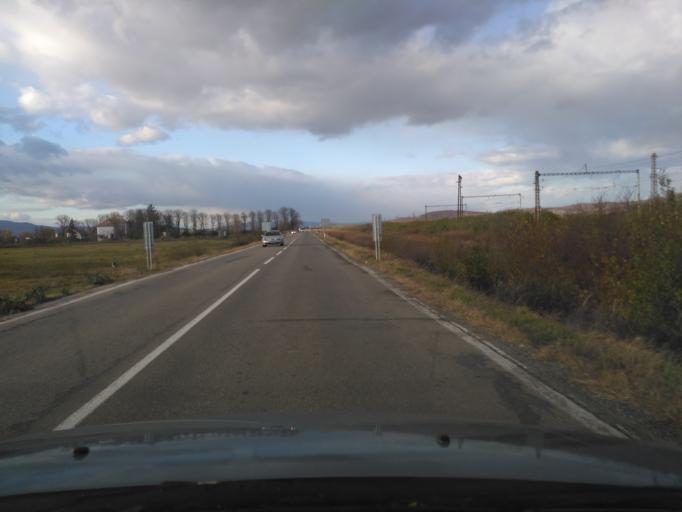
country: HU
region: Borsod-Abauj-Zemplen
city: Satoraljaujhely
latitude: 48.4127
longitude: 21.6656
